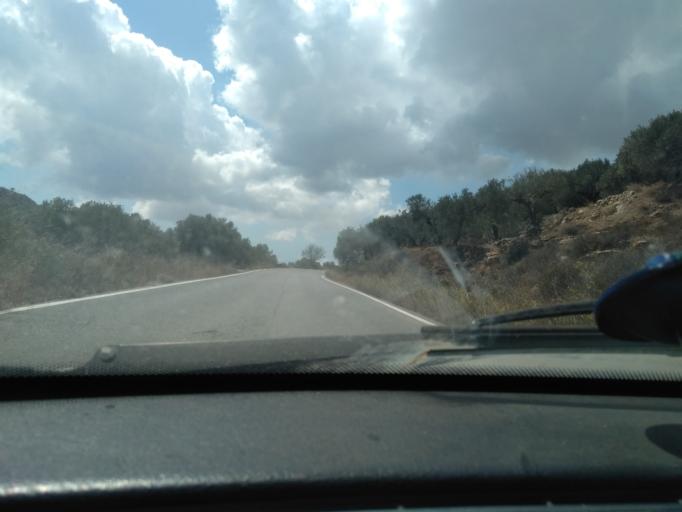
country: GR
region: Crete
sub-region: Nomos Lasithiou
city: Siteia
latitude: 35.1224
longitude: 26.0631
